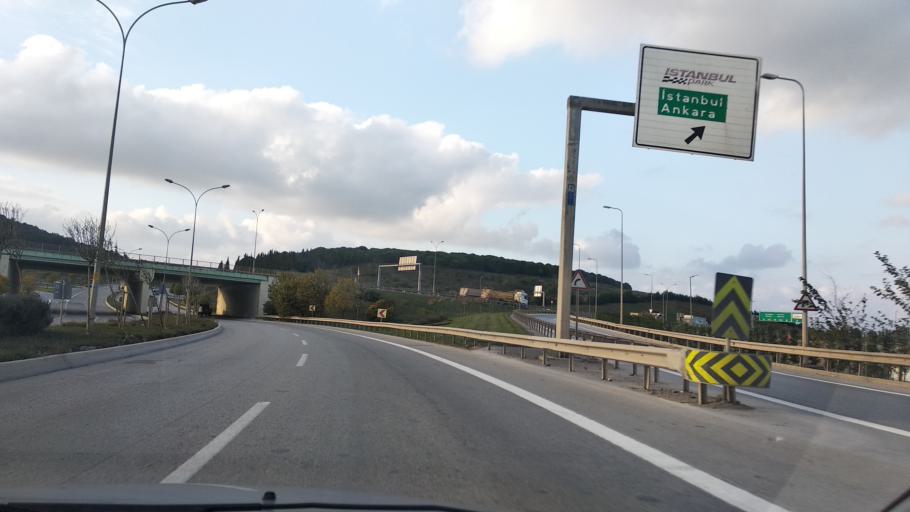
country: TR
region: Istanbul
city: Sultanbeyli
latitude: 40.9212
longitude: 29.3423
